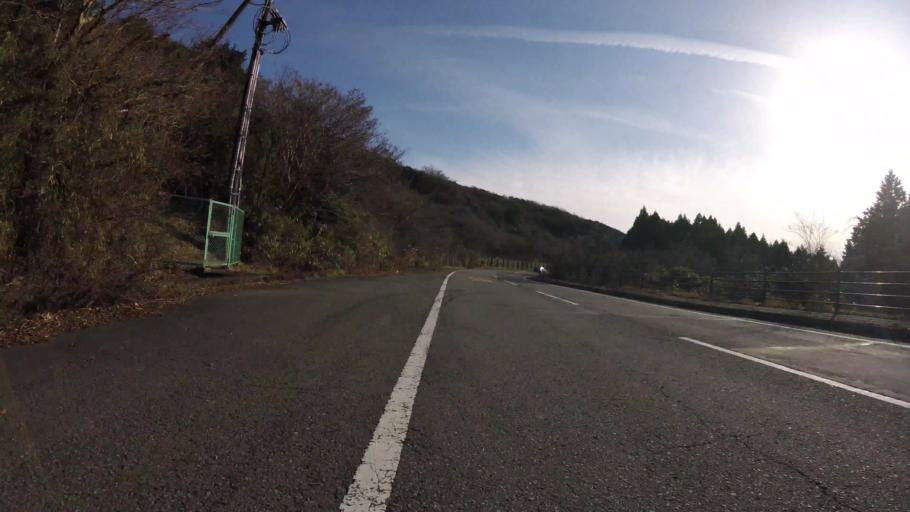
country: JP
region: Kanagawa
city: Hakone
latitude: 35.1735
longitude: 139.0215
